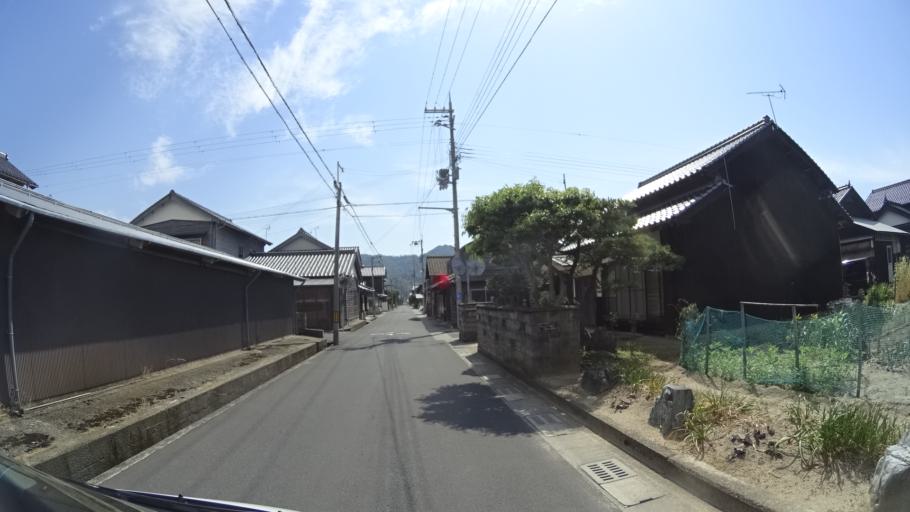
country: JP
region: Kyoto
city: Miyazu
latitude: 35.6861
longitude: 135.0269
